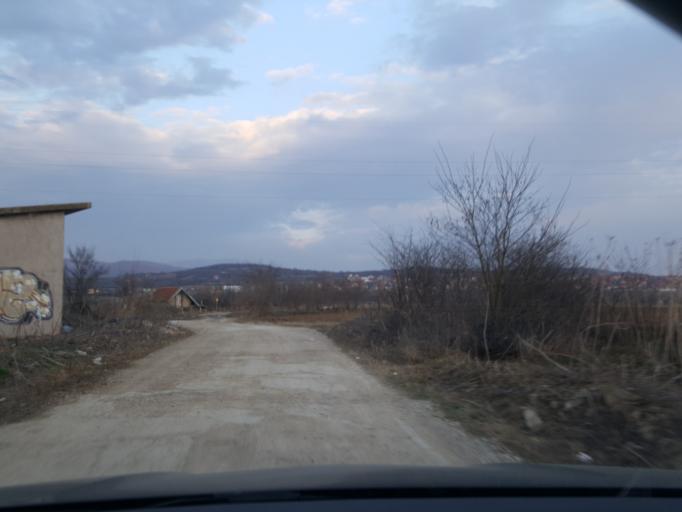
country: RS
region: Central Serbia
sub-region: Nisavski Okrug
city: Aleksinac
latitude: 43.5484
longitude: 21.6788
